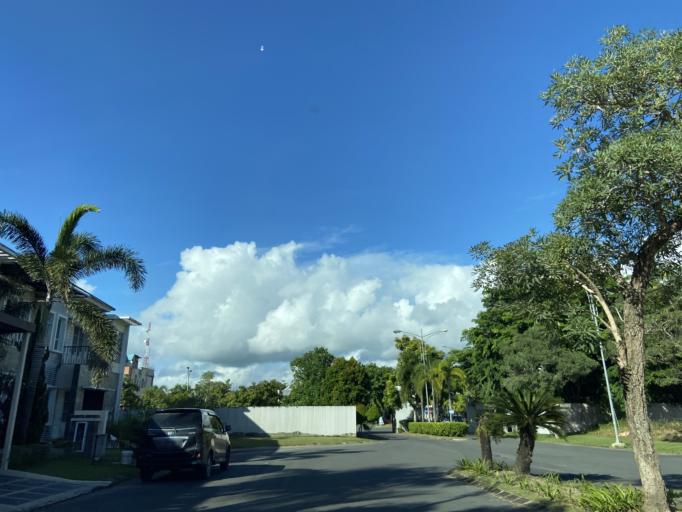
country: SG
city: Singapore
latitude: 1.0930
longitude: 104.0337
